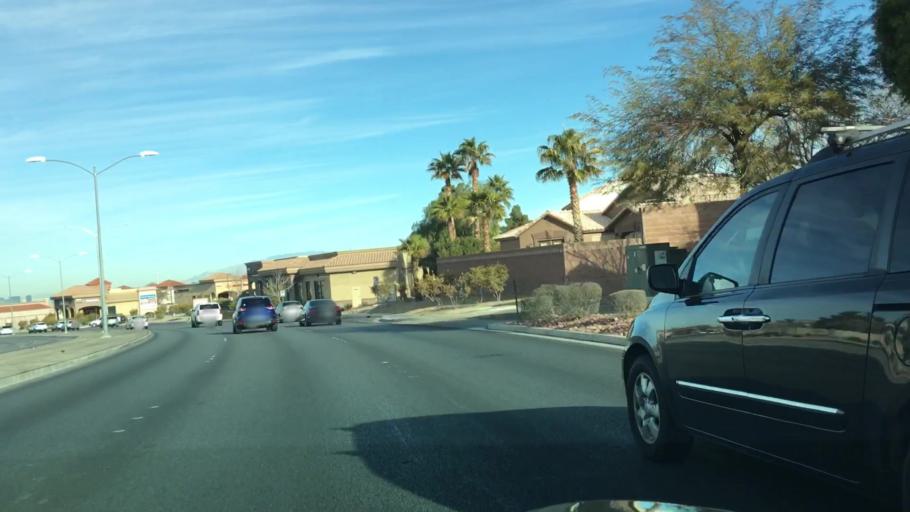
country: US
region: Nevada
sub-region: Clark County
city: Whitney
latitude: 35.9956
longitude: -115.1010
